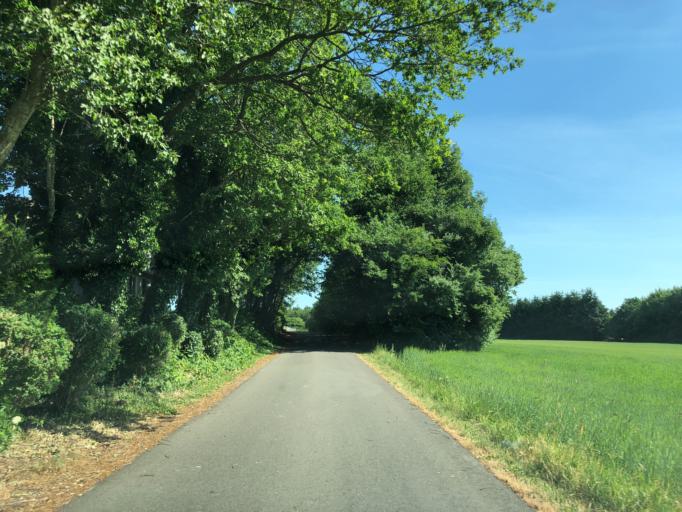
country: DK
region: Central Jutland
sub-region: Struer Kommune
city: Struer
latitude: 56.4304
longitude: 8.4407
